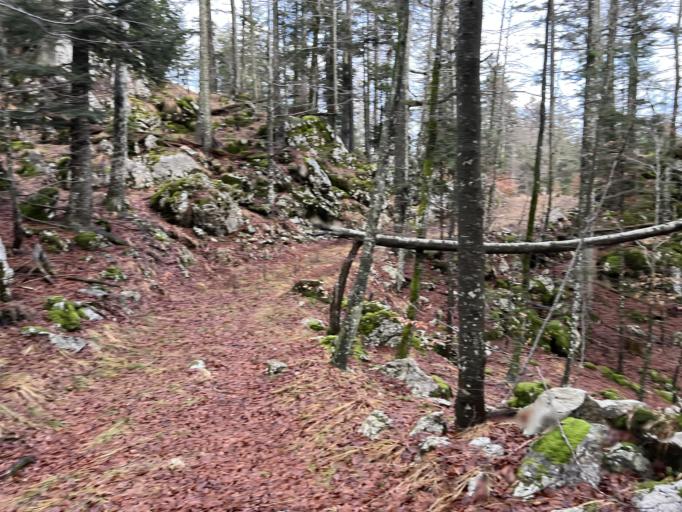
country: SI
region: Nova Gorica
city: Sempas
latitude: 45.9863
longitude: 13.8097
